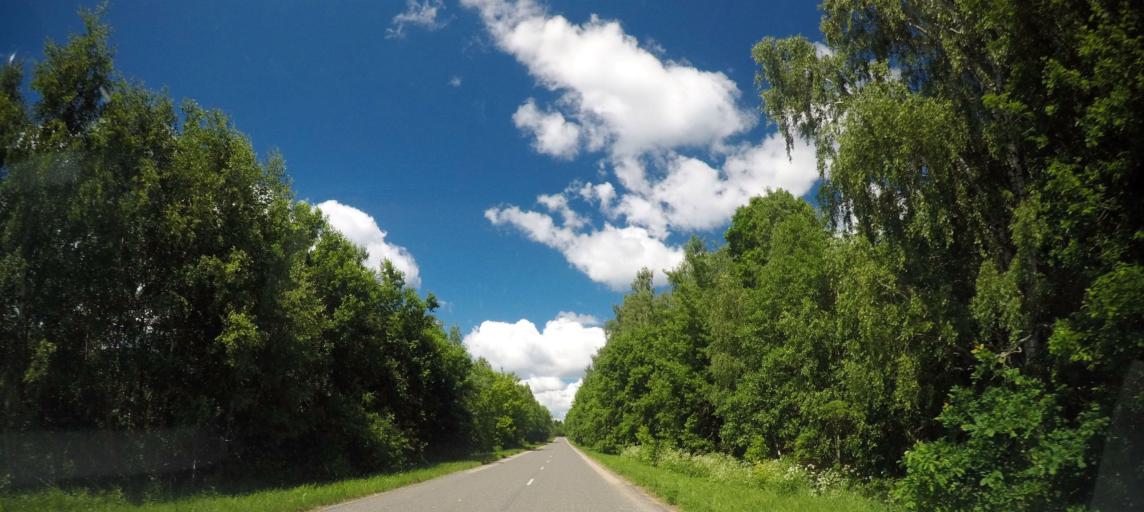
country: BY
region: Grodnenskaya
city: Hal'shany
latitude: 54.1807
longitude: 26.1008
